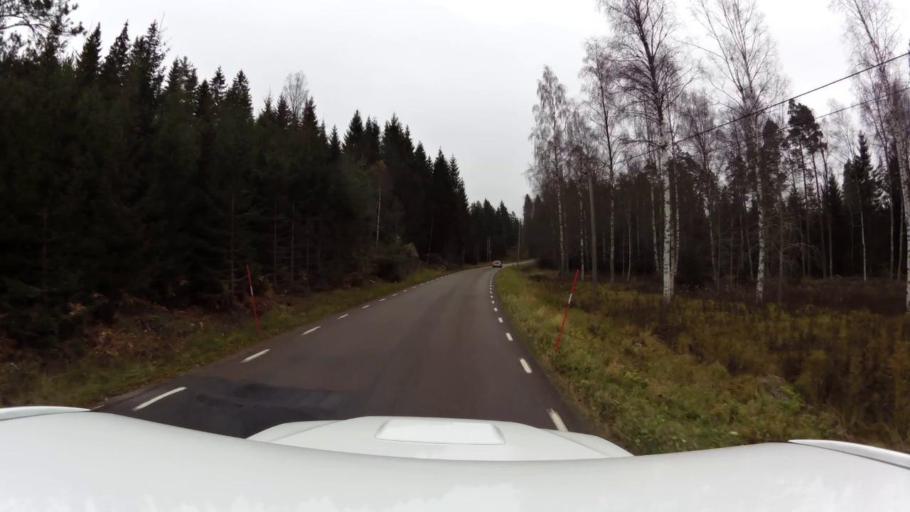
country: SE
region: OEstergoetland
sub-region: Linkopings Kommun
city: Vikingstad
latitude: 58.1333
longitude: 15.4232
